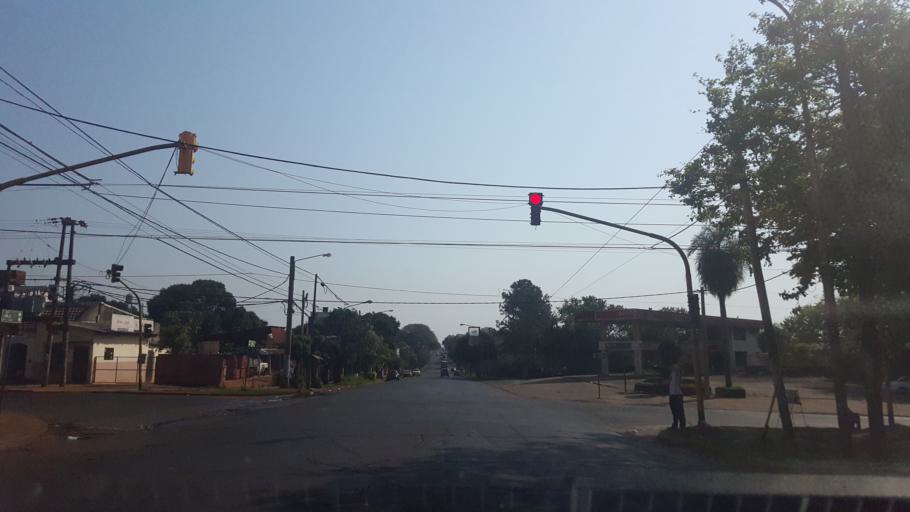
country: AR
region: Misiones
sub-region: Departamento de Capital
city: Posadas
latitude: -27.3837
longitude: -55.9074
